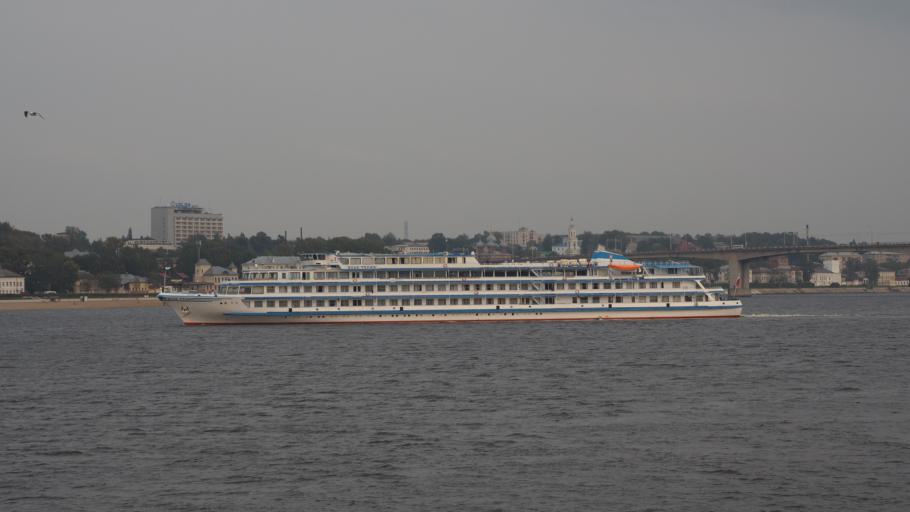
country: RU
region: Kostroma
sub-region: Kostromskoy Rayon
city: Kostroma
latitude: 57.7577
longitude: 40.9238
